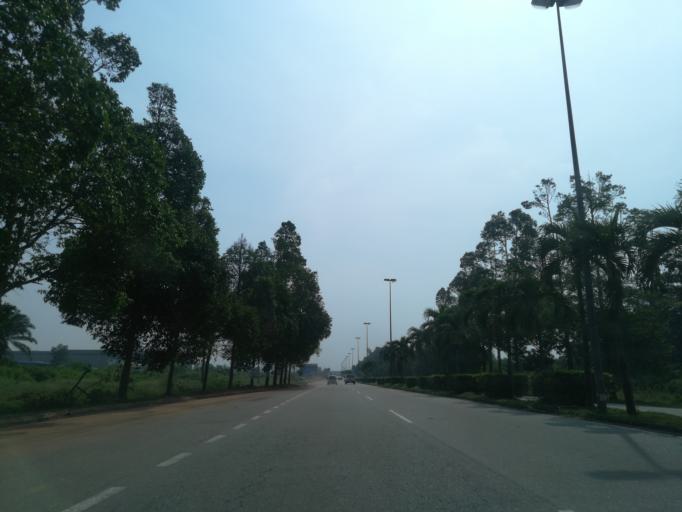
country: MY
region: Penang
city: Tasek Glugor
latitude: 5.4386
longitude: 100.5578
